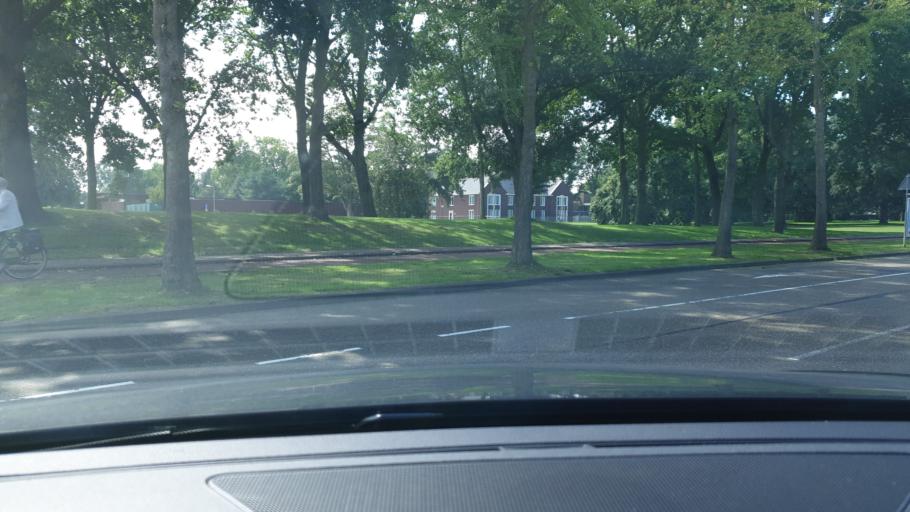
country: NL
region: Limburg
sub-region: Gemeente Venray
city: Venray
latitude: 51.5287
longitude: 5.9871
